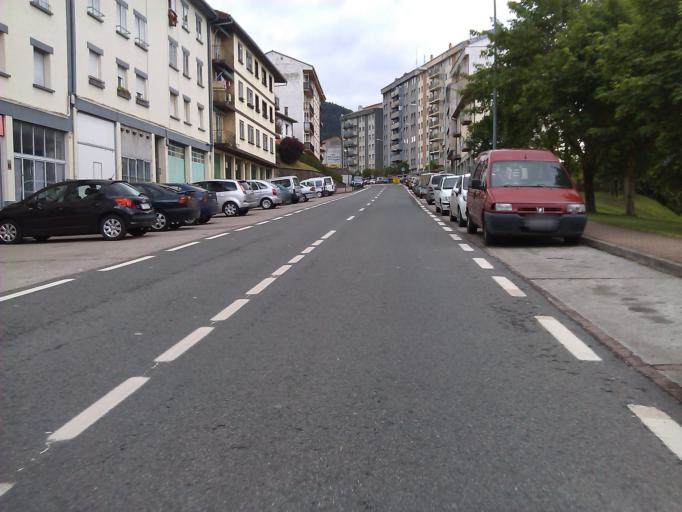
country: ES
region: Navarre
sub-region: Provincia de Navarra
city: Irurtzun
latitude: 42.9214
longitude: -1.8307
